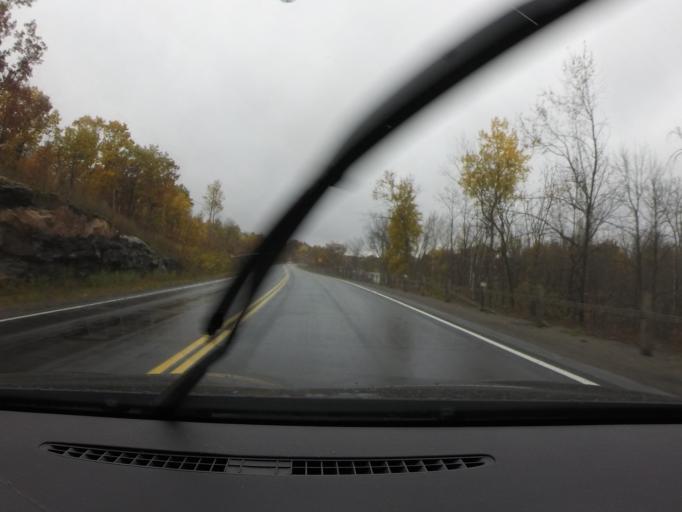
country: CA
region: Ontario
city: Deseronto
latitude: 44.5958
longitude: -77.1895
